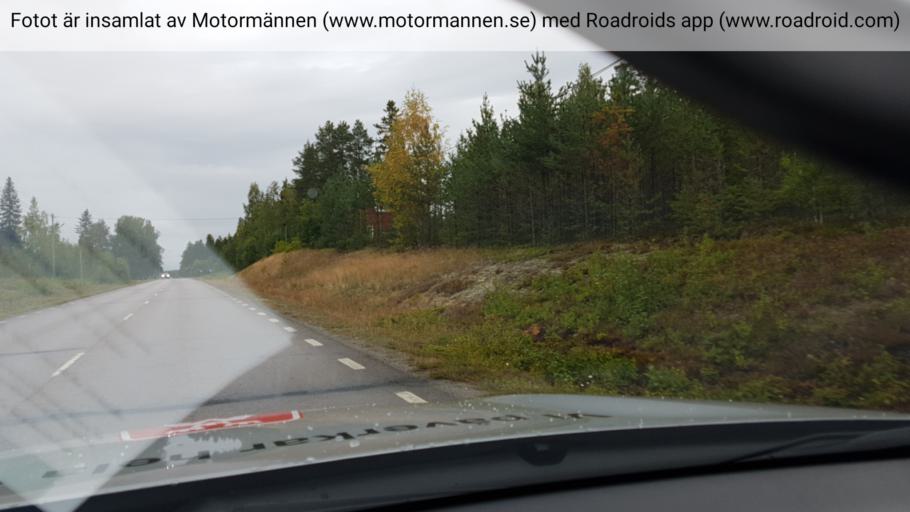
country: SE
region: Norrbotten
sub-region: Alvsbyns Kommun
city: AElvsbyn
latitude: 66.1069
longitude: 20.9347
